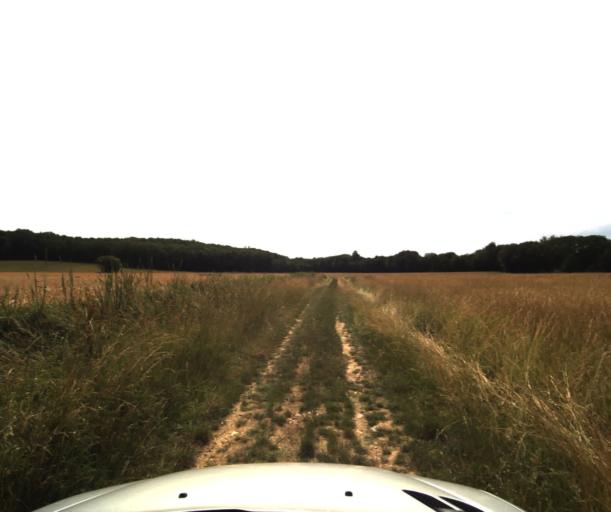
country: FR
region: Midi-Pyrenees
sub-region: Departement de la Haute-Garonne
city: Saint-Lys
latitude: 43.4857
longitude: 1.2070
